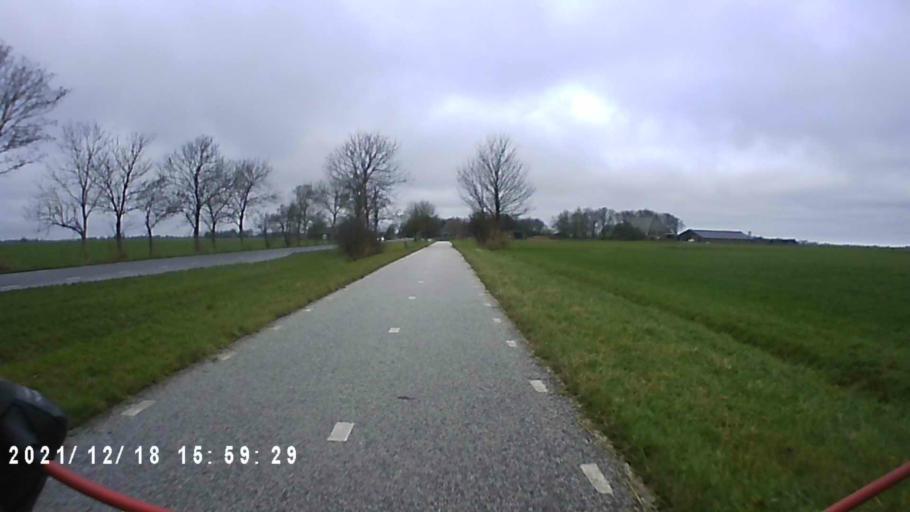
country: NL
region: Friesland
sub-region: Gemeente Dongeradeel
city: Anjum
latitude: 53.3397
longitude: 6.0901
